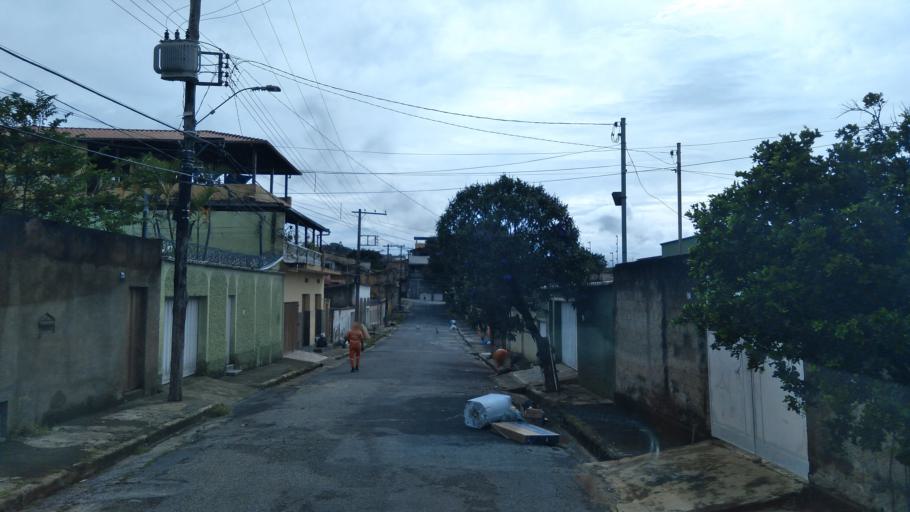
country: BR
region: Minas Gerais
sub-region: Belo Horizonte
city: Belo Horizonte
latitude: -19.9008
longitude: -43.9031
